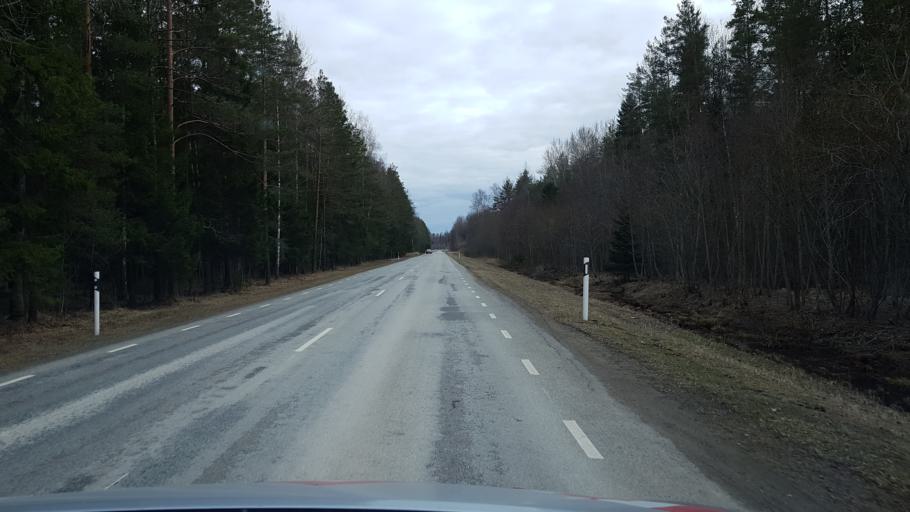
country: EE
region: Ida-Virumaa
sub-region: Toila vald
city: Toila
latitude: 59.3817
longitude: 27.5066
